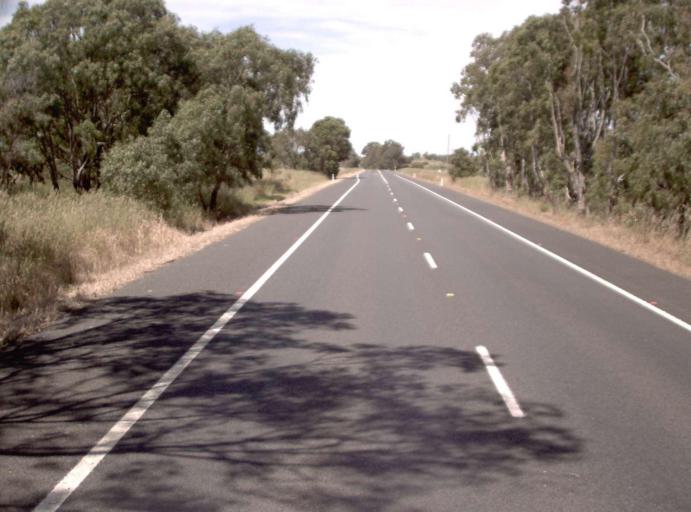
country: AU
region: Victoria
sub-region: Wellington
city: Heyfield
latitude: -38.1101
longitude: 146.8894
